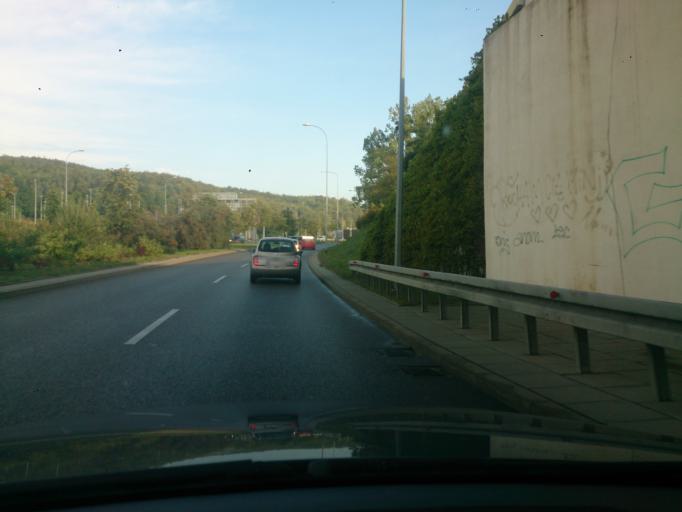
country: PL
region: Pomeranian Voivodeship
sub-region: Gdynia
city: Gdynia
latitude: 54.4991
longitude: 18.5337
